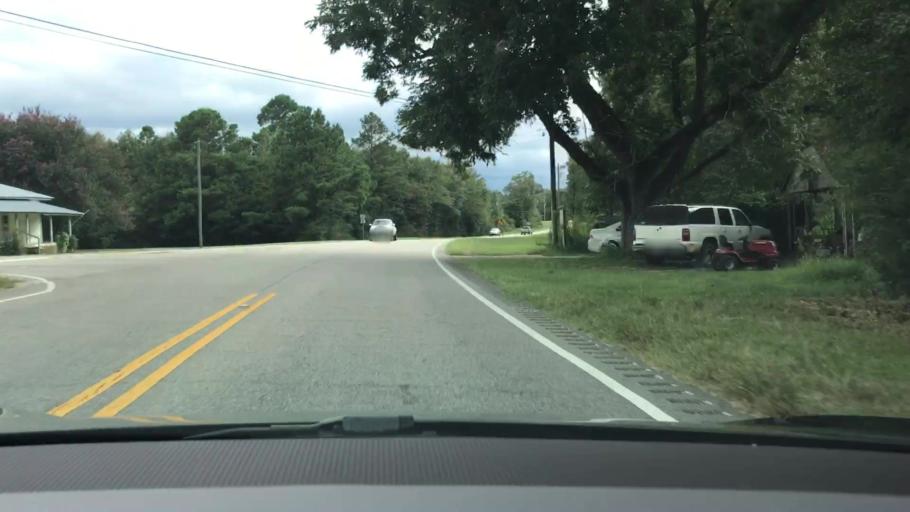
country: US
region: Alabama
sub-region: Coffee County
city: Elba
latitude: 31.5415
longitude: -86.0232
